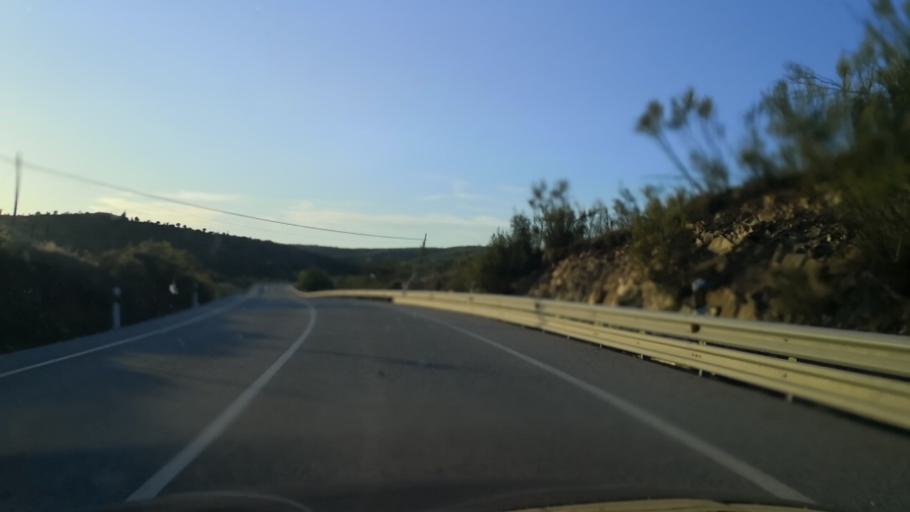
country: ES
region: Extremadura
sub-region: Provincia de Caceres
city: Valencia de Alcantara
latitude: 39.4699
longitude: -7.2081
